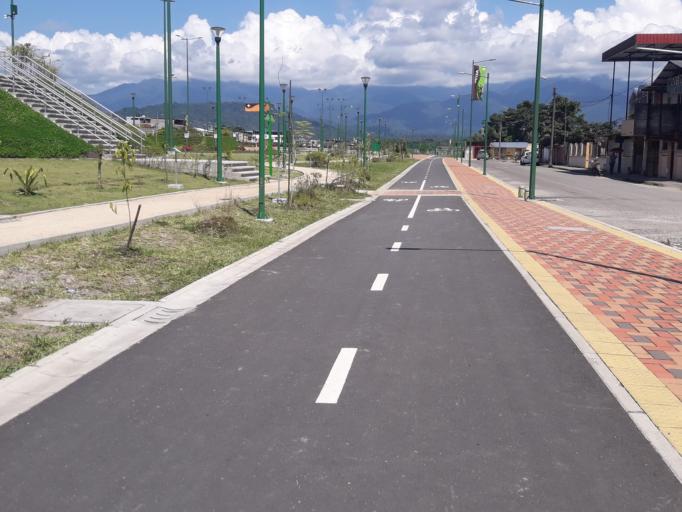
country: EC
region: Napo
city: Tena
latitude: -0.9869
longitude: -77.8166
